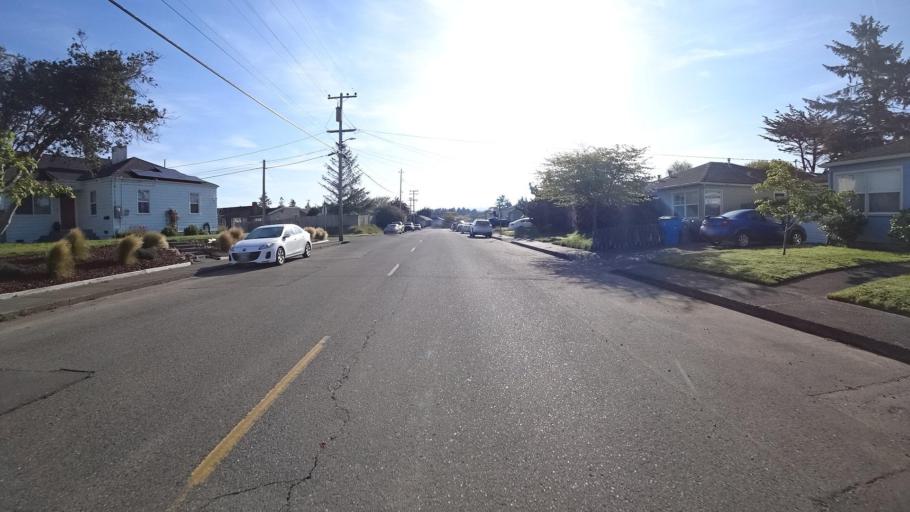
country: US
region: California
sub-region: Humboldt County
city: Bayview
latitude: 40.7739
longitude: -124.1766
